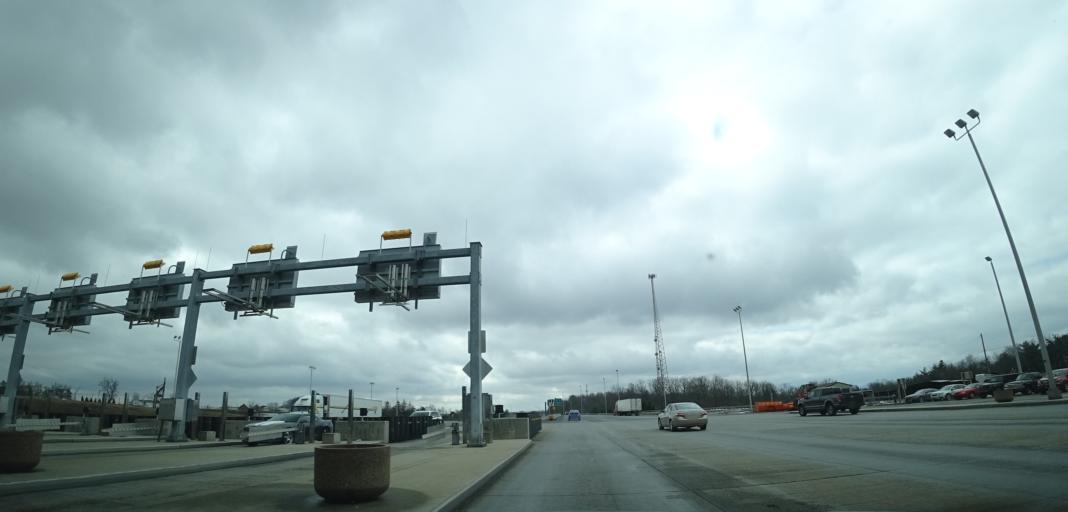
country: US
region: Pennsylvania
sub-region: Bedford County
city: Earlston
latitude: 39.9898
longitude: -78.2524
